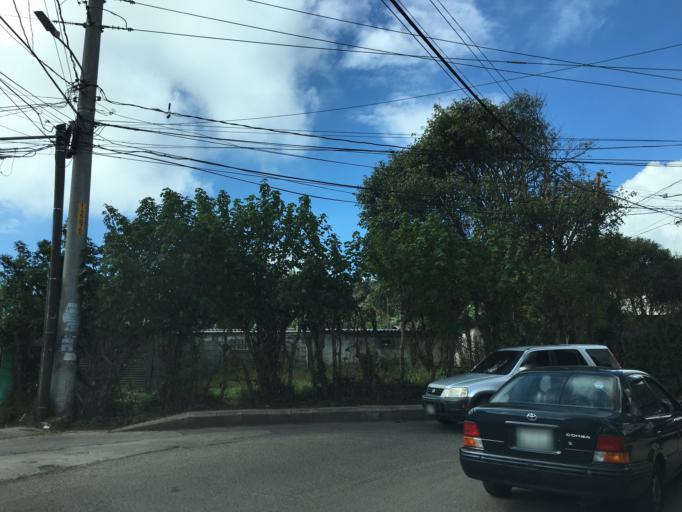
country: GT
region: Guatemala
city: San Jose Pinula
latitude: 14.5595
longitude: -90.4381
